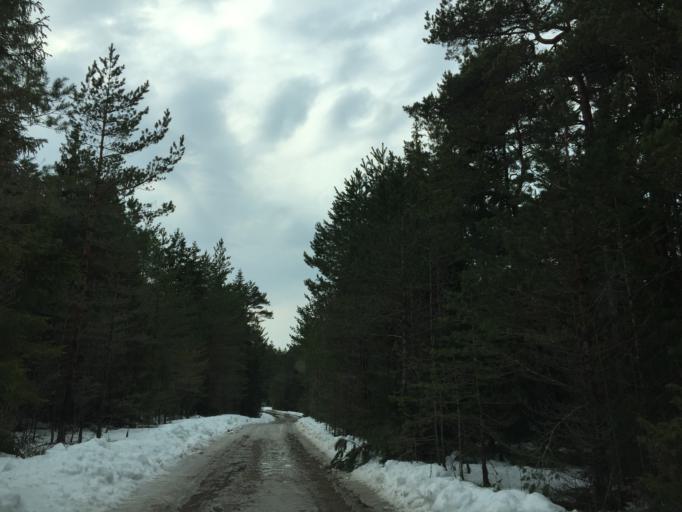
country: EE
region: Saare
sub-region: Kuressaare linn
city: Kuressaare
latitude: 58.4385
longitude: 22.1318
